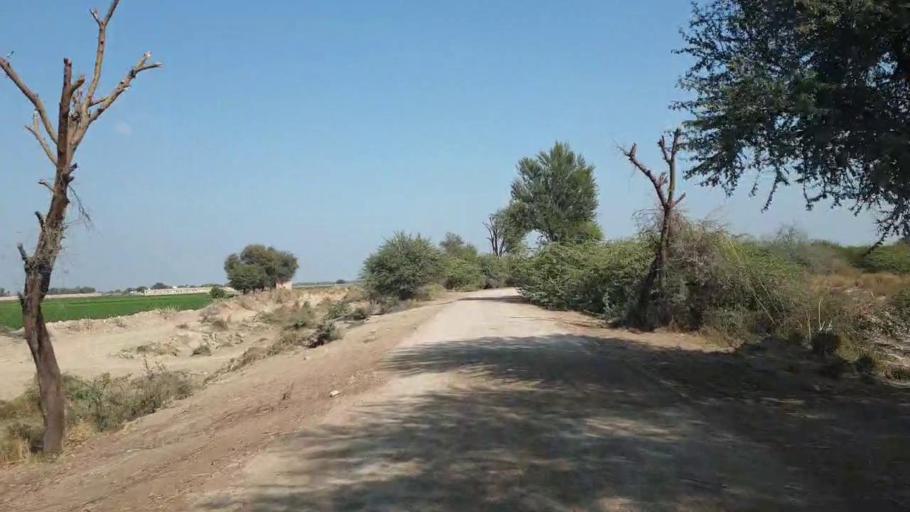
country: PK
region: Sindh
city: Shahpur Chakar
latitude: 26.0566
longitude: 68.5868
